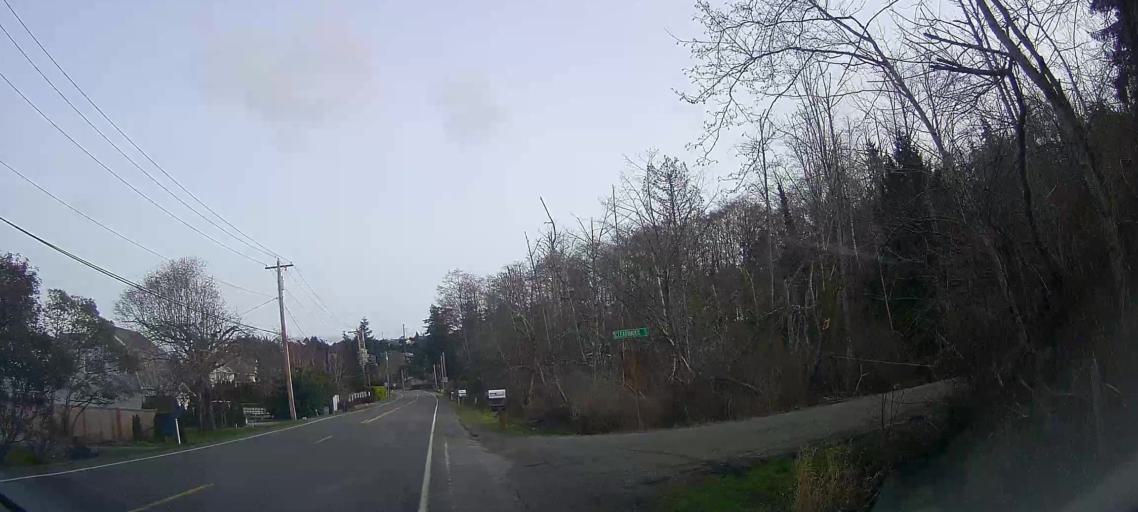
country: US
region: Washington
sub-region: Island County
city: Camano
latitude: 48.2502
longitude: -122.4850
